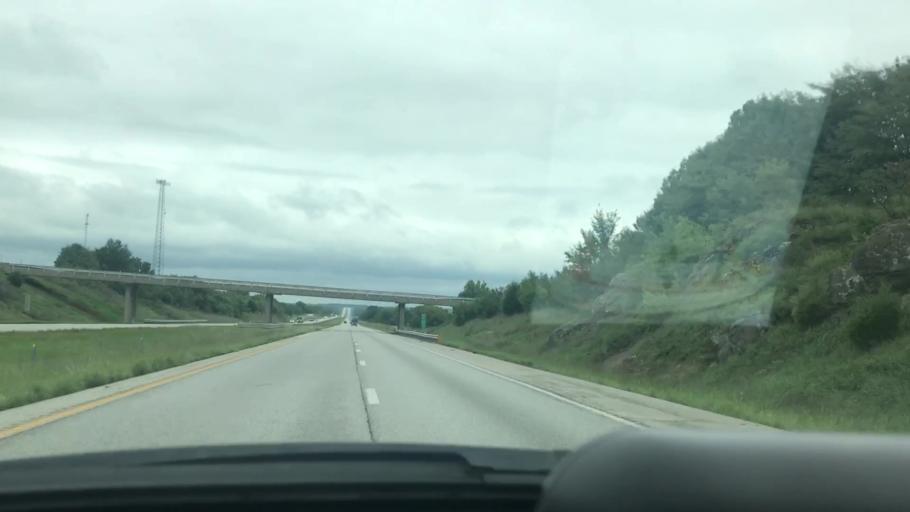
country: US
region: Missouri
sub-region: Lawrence County
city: Mount Vernon
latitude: 37.1541
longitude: -93.6974
